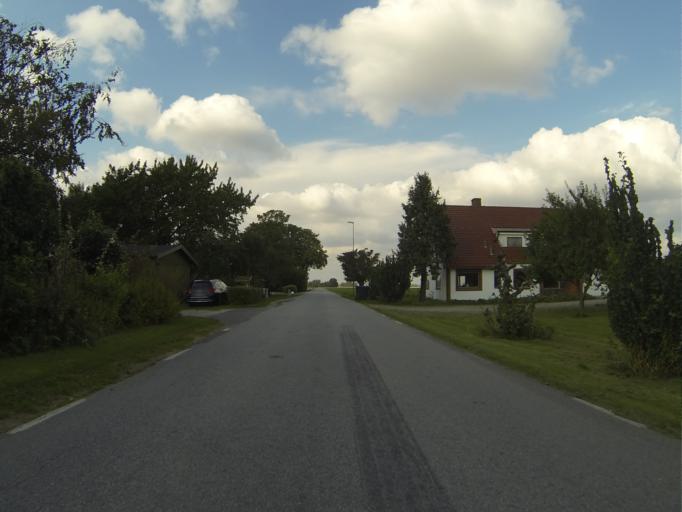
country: SE
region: Skane
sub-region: Lunds Kommun
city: Lund
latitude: 55.7680
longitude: 13.1781
